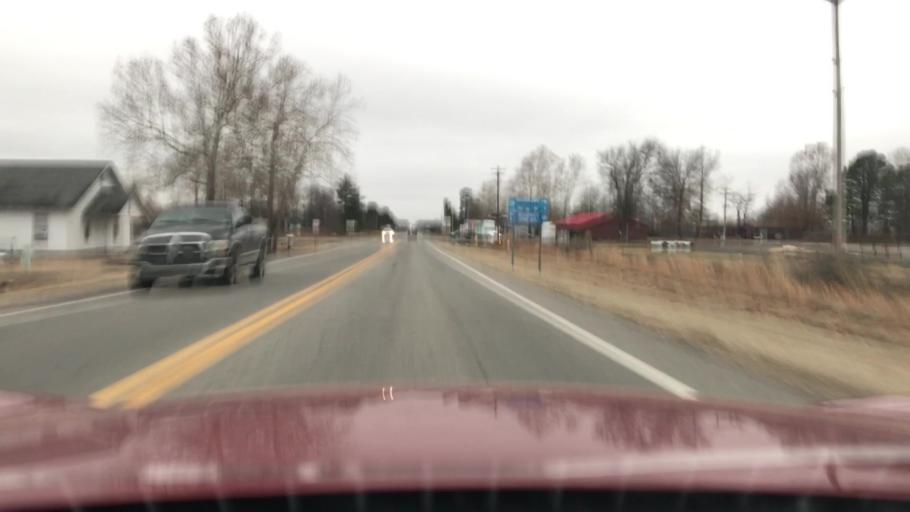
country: US
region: Oklahoma
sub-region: Sequoyah County
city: Sallisaw
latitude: 35.5080
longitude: -94.7722
